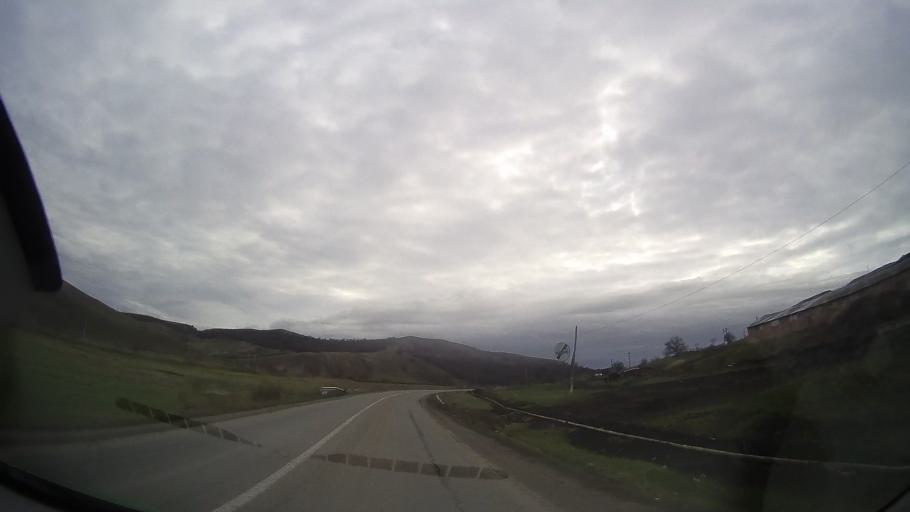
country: RO
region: Bistrita-Nasaud
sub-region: Comuna Budesti
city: Budesti
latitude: 46.8687
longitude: 24.2458
